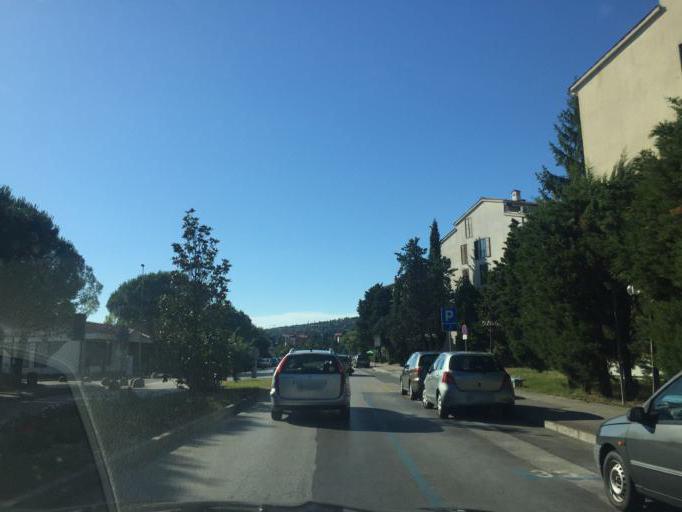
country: SI
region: Piran-Pirano
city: Lucija
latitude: 45.5038
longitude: 13.6038
